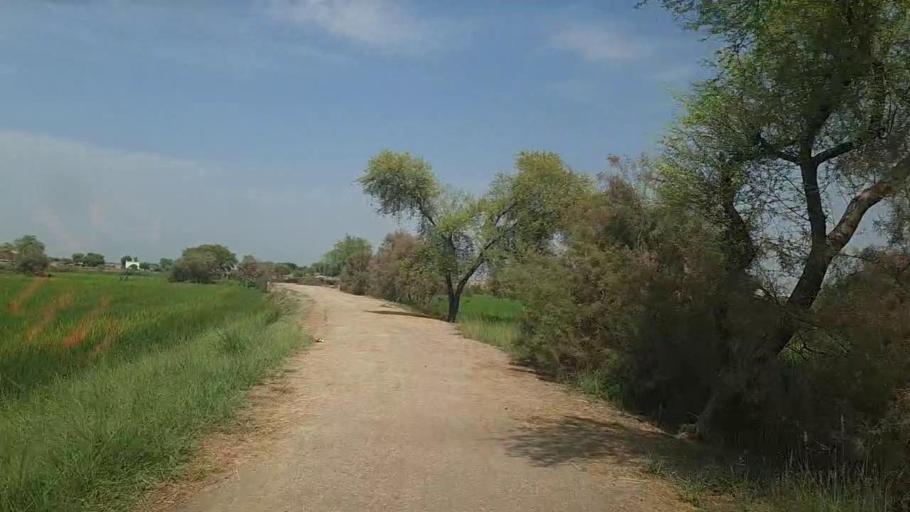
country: PK
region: Sindh
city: Thul
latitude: 28.3050
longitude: 68.6823
